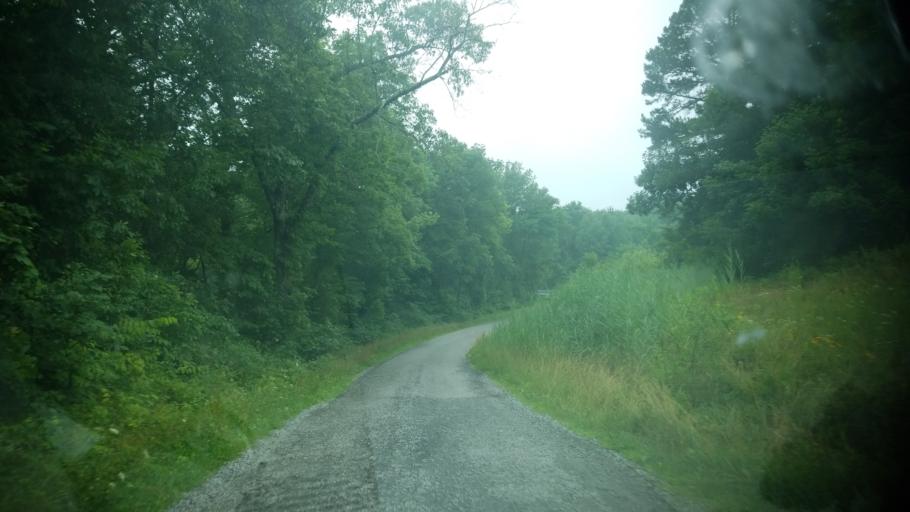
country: US
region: Illinois
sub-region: Clay County
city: Flora
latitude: 38.5734
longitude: -88.3662
